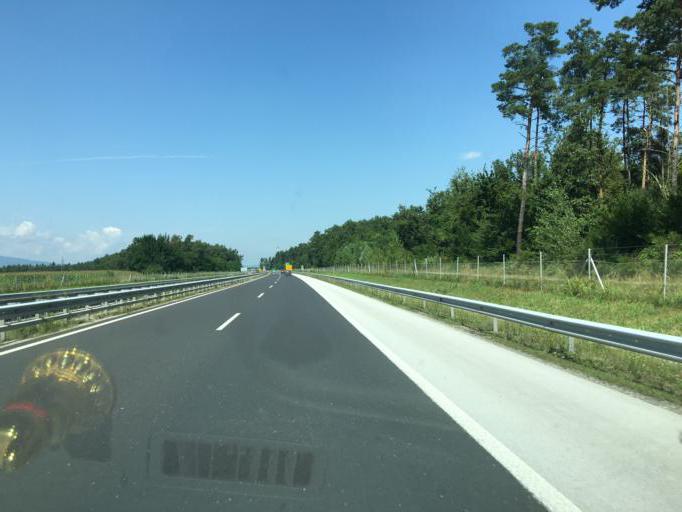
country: SI
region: Kidricevo
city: Kidricevo
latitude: 46.4325
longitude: 15.7920
